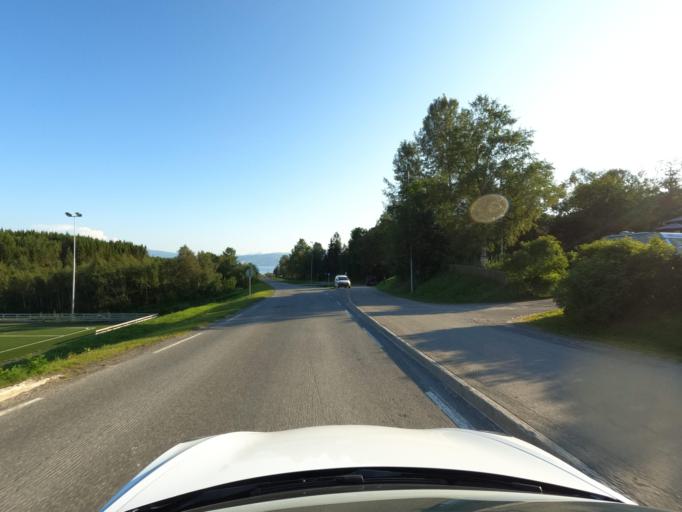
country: NO
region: Nordland
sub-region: Evenes
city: Randa
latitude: 68.4884
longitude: 16.8993
